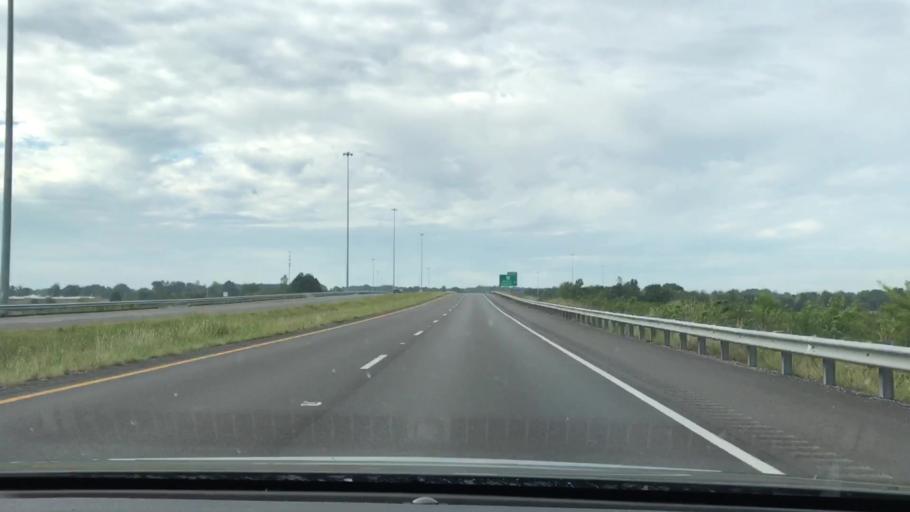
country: US
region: Kentucky
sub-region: Marshall County
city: Benton
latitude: 36.8757
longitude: -88.3611
